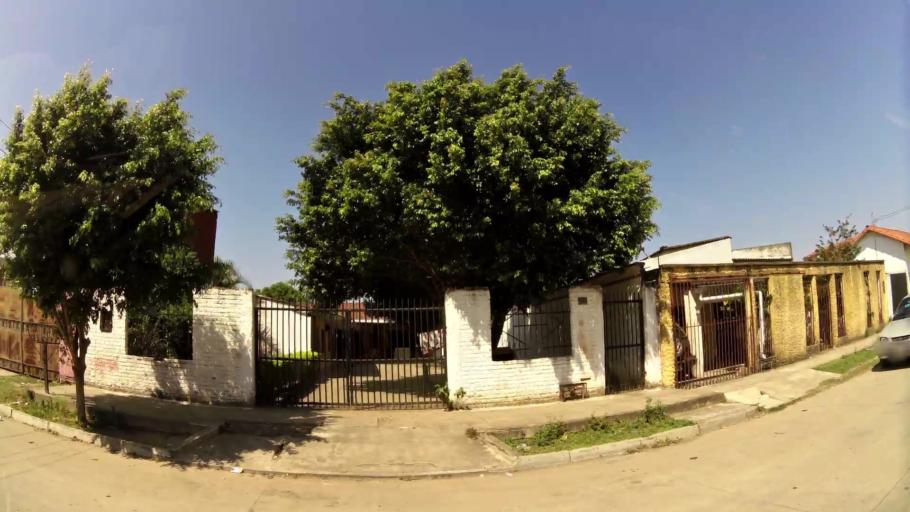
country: BO
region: Santa Cruz
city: Santa Cruz de la Sierra
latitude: -17.7453
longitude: -63.1554
